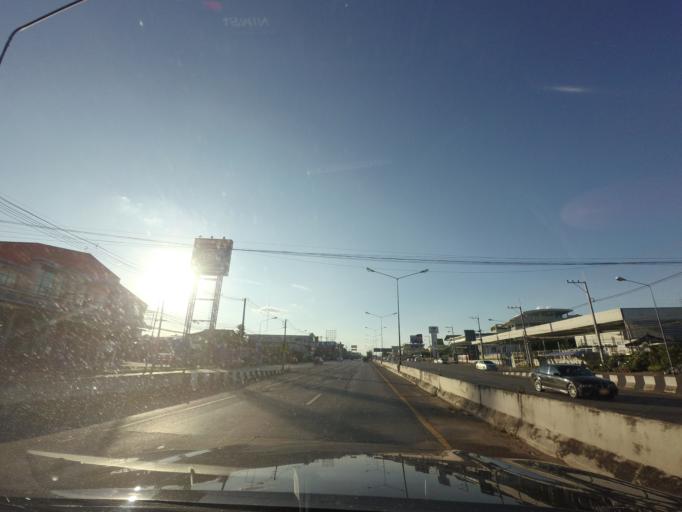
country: TH
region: Changwat Udon Thani
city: Udon Thani
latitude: 17.3886
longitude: 102.8231
